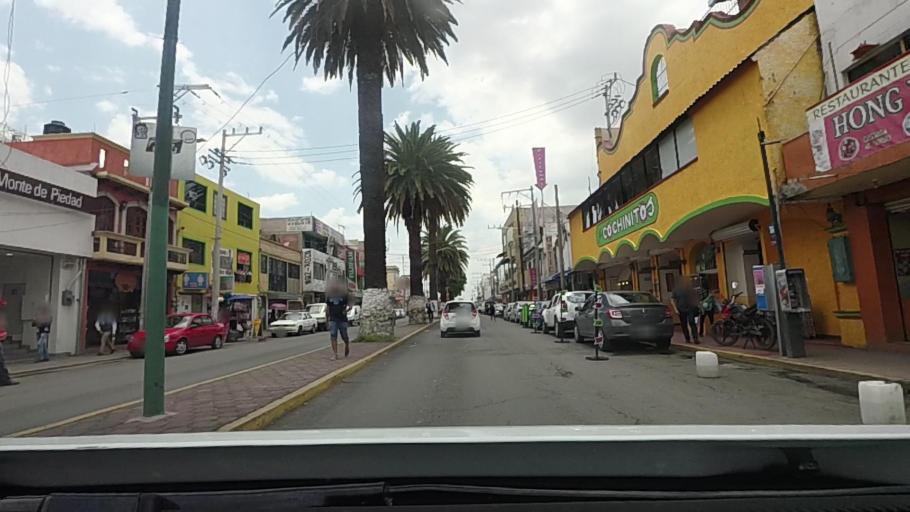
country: MX
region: Mexico
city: Chalco de Diaz Covarrubias
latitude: 19.2612
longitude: -98.8976
